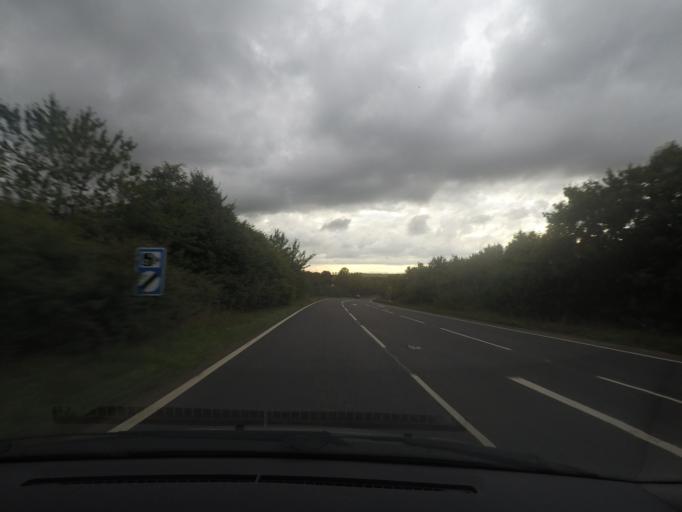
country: GB
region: England
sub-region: Lincolnshire
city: Louth
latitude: 53.3527
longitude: -0.0220
